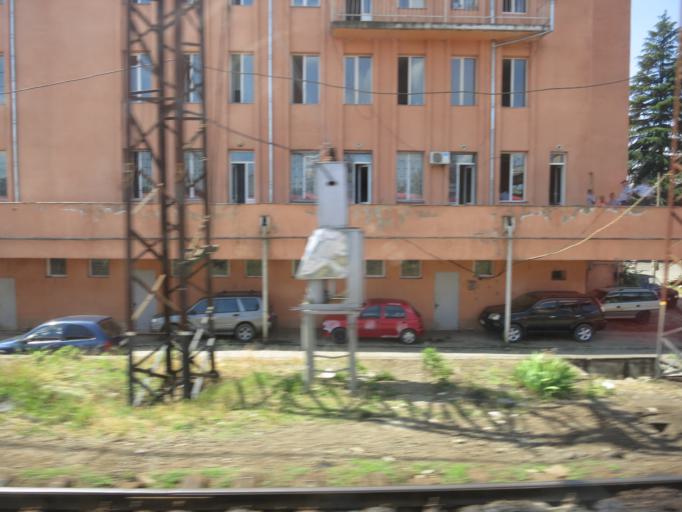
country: GE
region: Imereti
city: Zestap'oni
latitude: 42.1073
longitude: 43.0332
